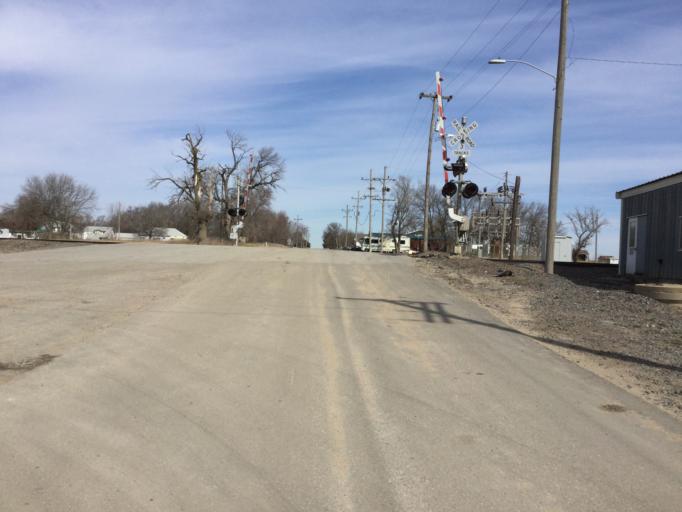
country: US
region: Kansas
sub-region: Marshall County
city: Marysville
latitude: 39.8892
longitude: -96.7124
